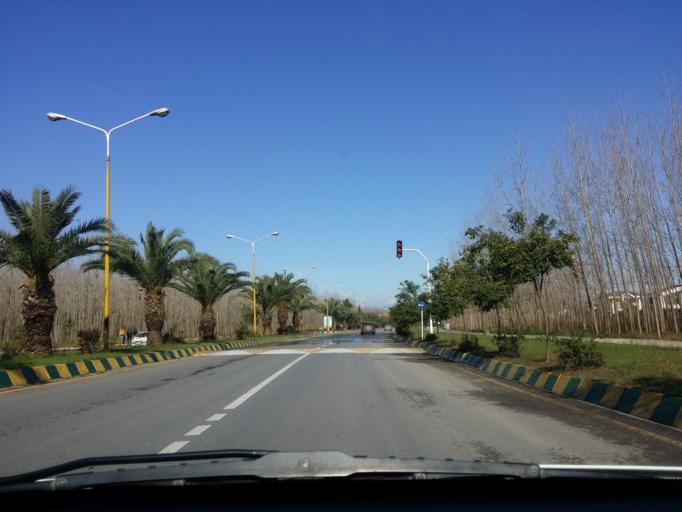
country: IR
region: Mazandaran
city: Chalus
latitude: 36.6723
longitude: 51.3068
